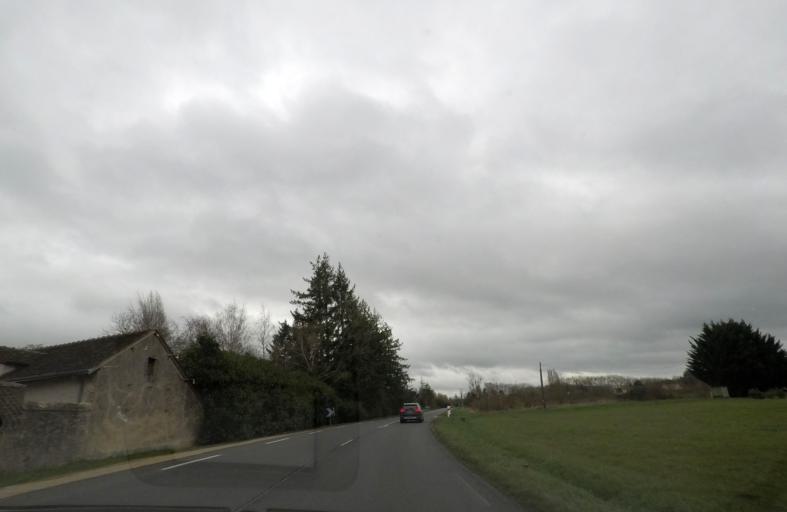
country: FR
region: Centre
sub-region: Departement du Loir-et-Cher
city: Cour-Cheverny
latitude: 47.5273
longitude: 1.4307
